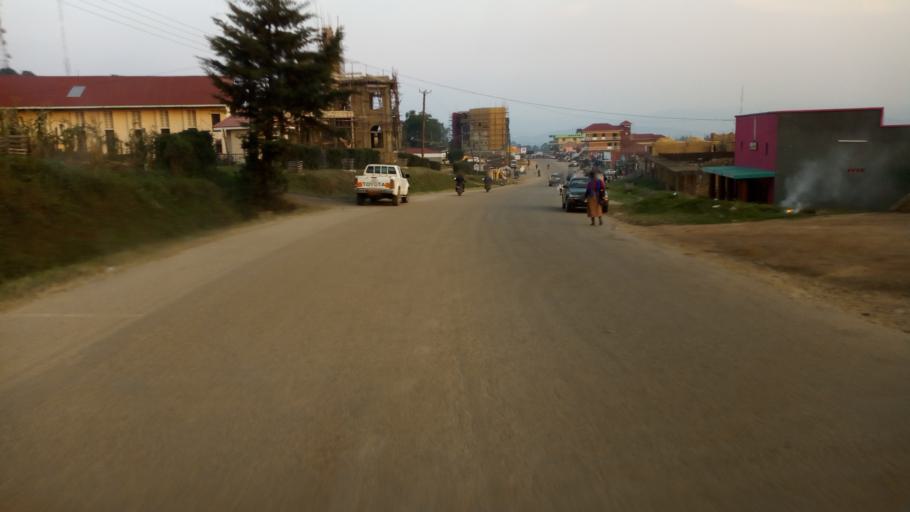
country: UG
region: Western Region
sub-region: Rukungiri District
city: Rukungiri
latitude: -0.7854
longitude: 29.9265
